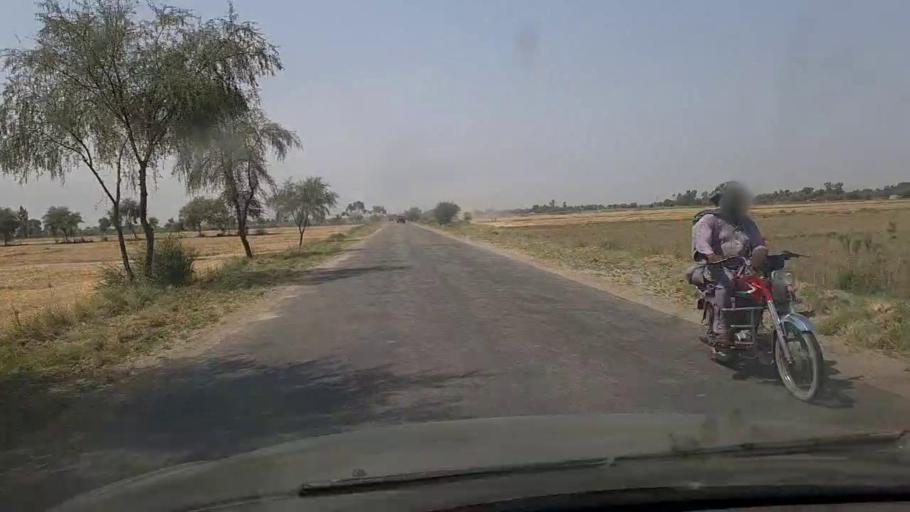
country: PK
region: Sindh
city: Khanpur
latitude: 27.8595
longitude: 69.4346
